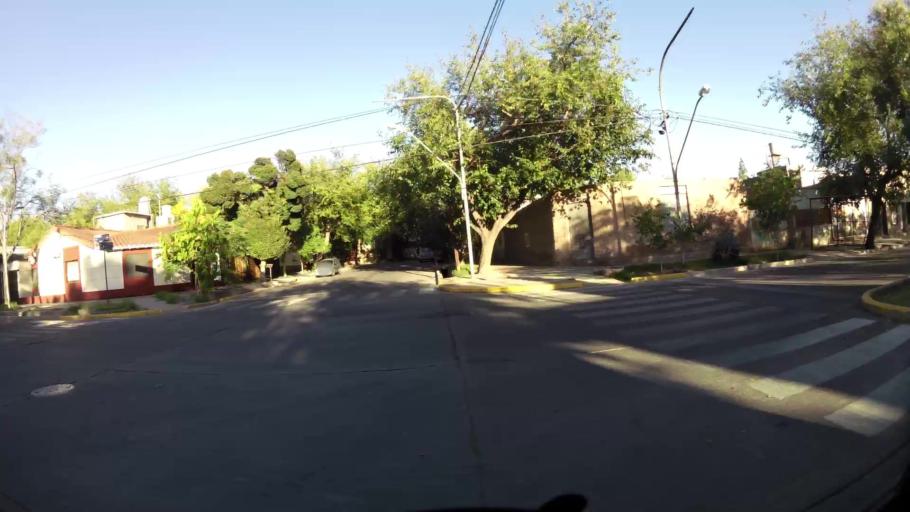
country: AR
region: Mendoza
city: Las Heras
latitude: -32.8683
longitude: -68.8390
